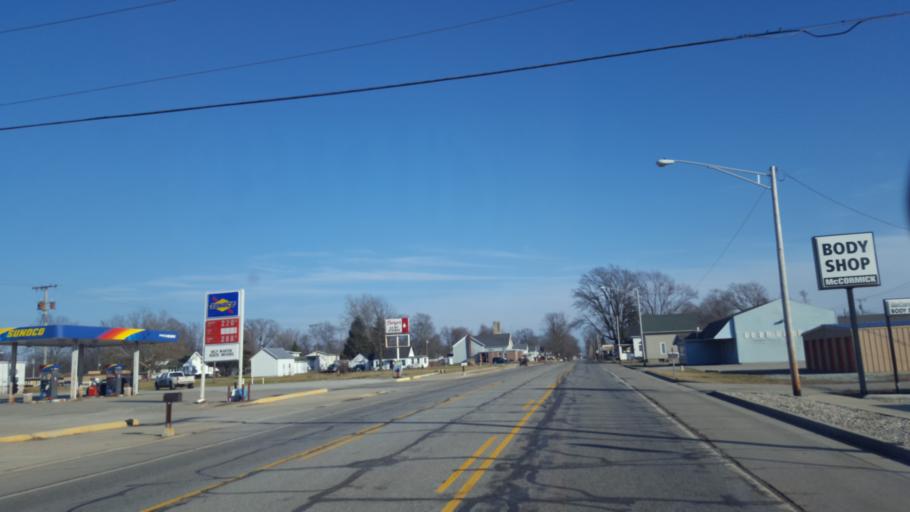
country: US
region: Indiana
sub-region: Elkhart County
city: Nappanee
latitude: 41.4427
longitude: -86.0140
